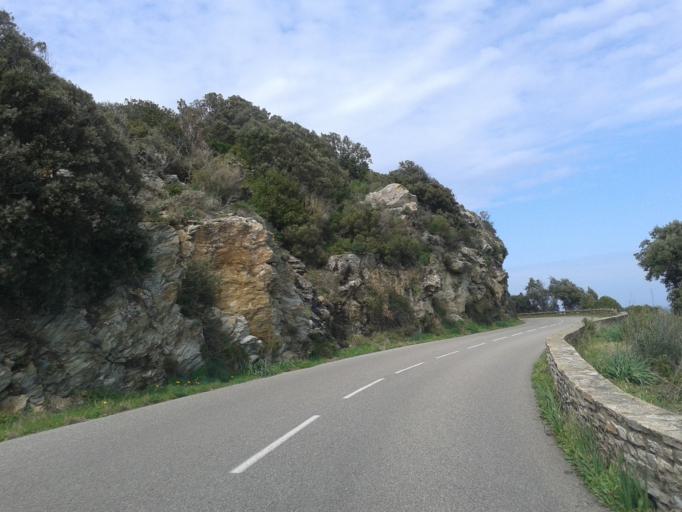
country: FR
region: Corsica
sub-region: Departement de la Haute-Corse
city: Brando
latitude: 42.9370
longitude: 9.4678
